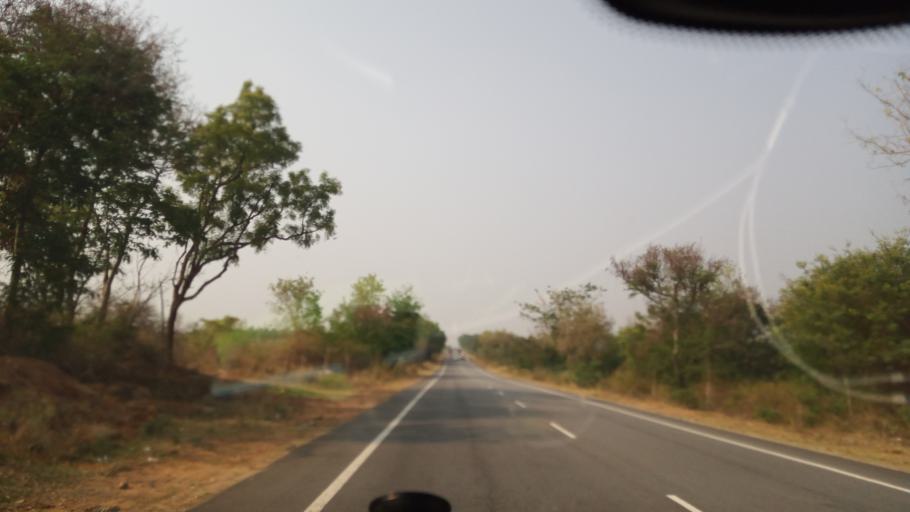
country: IN
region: Karnataka
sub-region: Mandya
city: Belluru
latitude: 12.9238
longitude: 76.7485
